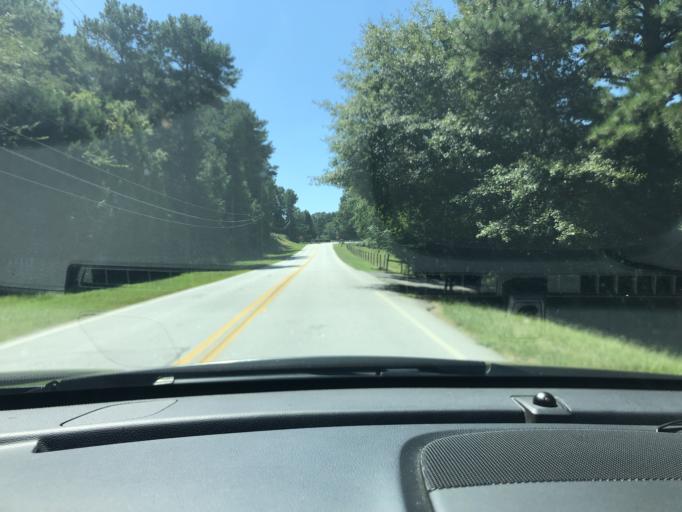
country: US
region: Georgia
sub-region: Gwinnett County
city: Grayson
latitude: 33.8979
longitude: -83.8998
